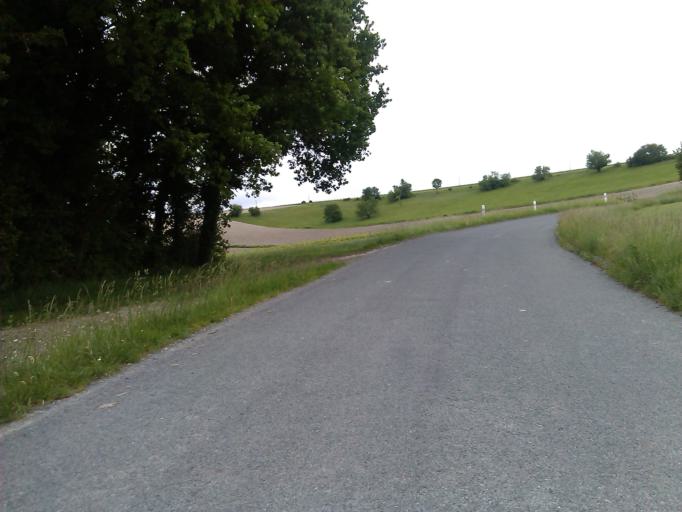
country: FR
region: Poitou-Charentes
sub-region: Departement de la Charente
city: Chateauneuf-sur-Charente
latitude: 45.5526
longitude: -0.0690
